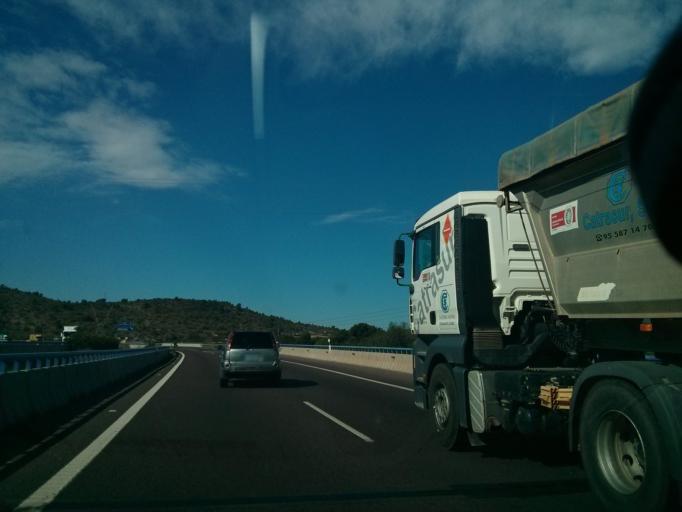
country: ES
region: Valencia
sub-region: Provincia de Castello
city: Chilches
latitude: 39.8079
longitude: -0.2195
